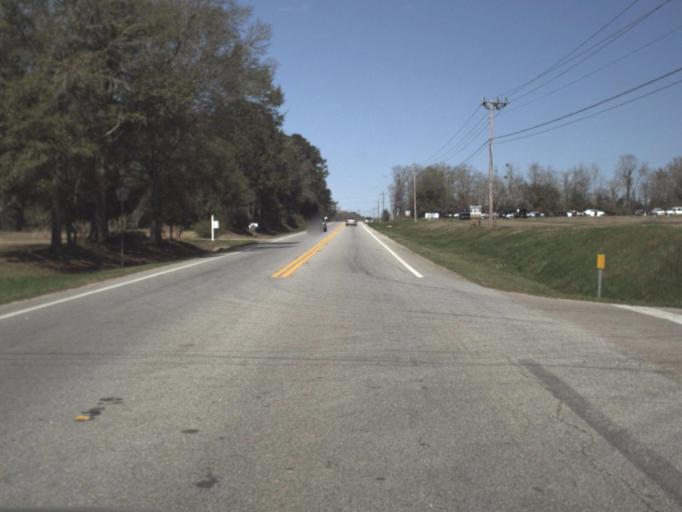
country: US
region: Florida
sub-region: Gadsden County
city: Quincy
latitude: 30.6441
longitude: -84.6003
